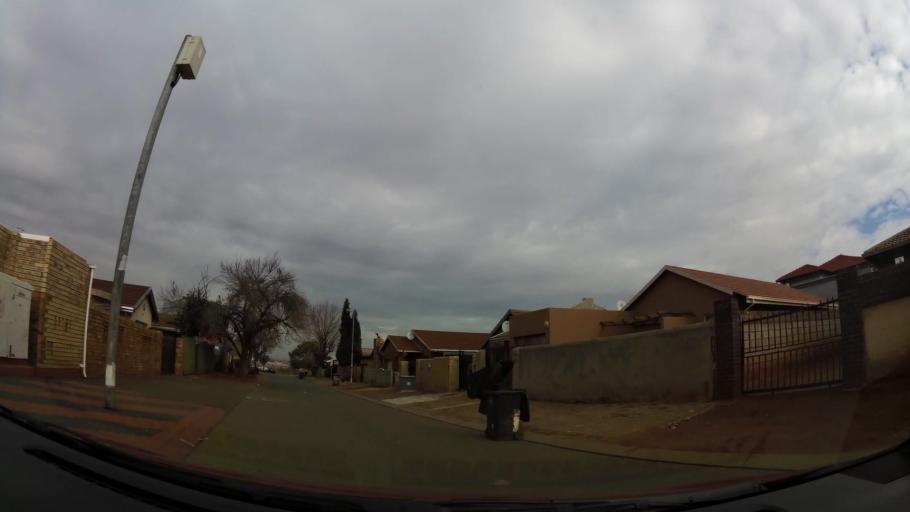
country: ZA
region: Gauteng
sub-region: City of Johannesburg Metropolitan Municipality
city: Soweto
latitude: -26.2748
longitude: 27.8313
